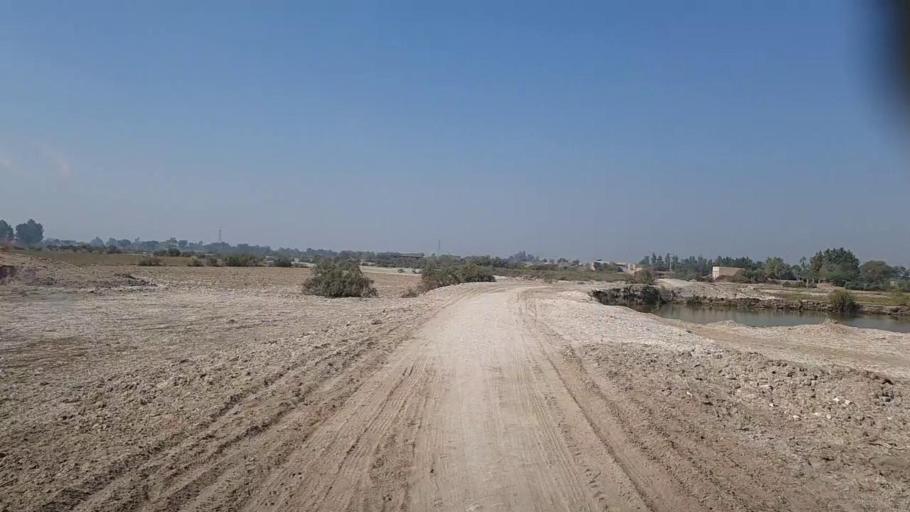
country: PK
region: Sindh
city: Khairpur
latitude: 27.9931
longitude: 69.6910
